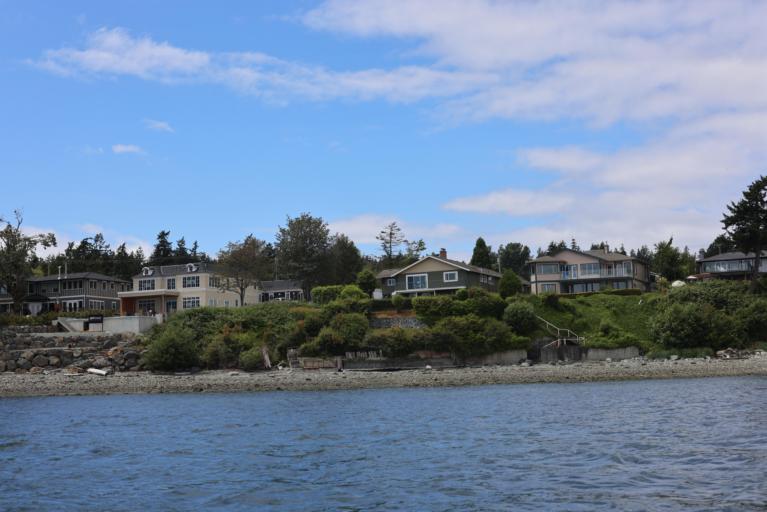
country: CA
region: British Columbia
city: North Saanich
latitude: 48.6179
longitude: -123.4008
